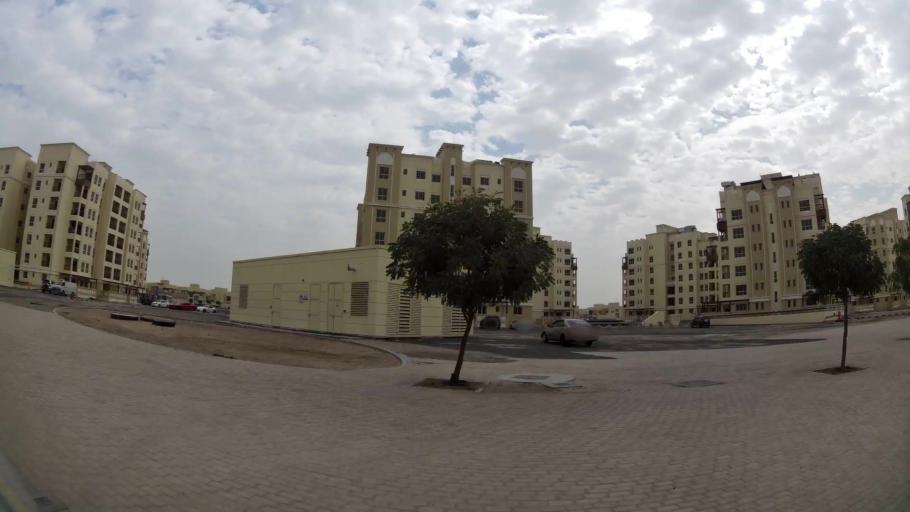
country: AE
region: Abu Dhabi
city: Abu Dhabi
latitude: 24.3114
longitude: 54.6214
